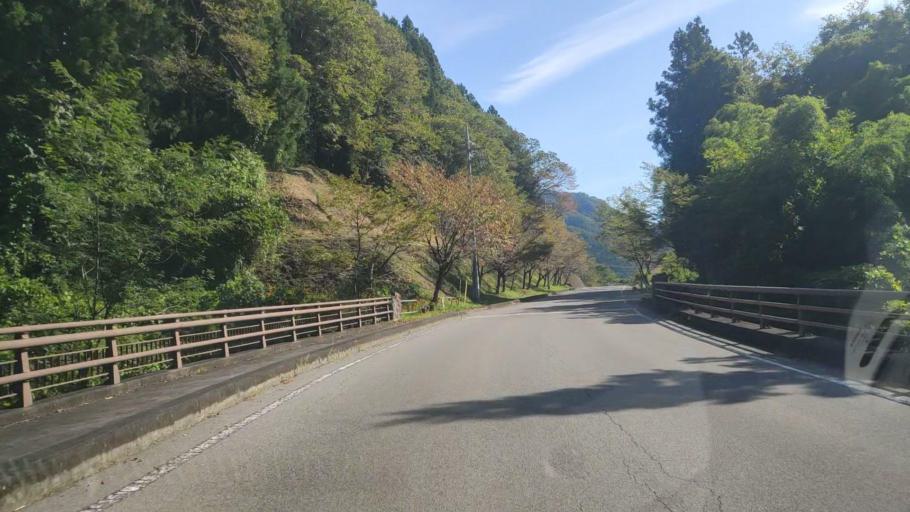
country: JP
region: Gunma
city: Nakanojomachi
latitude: 36.6222
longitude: 138.7670
